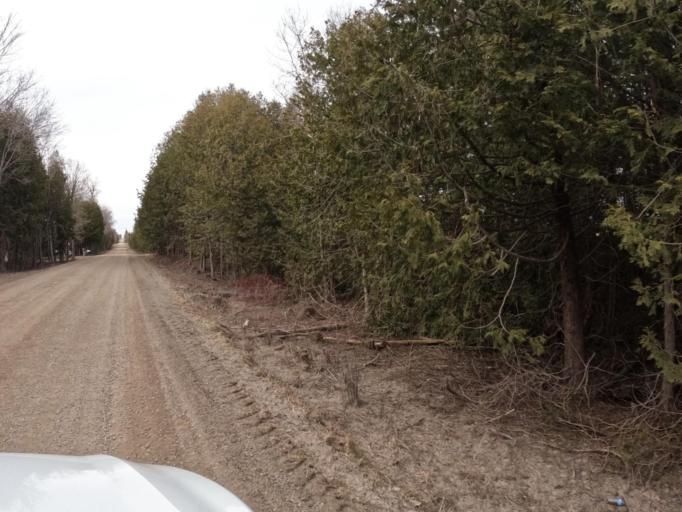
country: CA
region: Ontario
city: Shelburne
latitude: 43.9378
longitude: -80.2594
